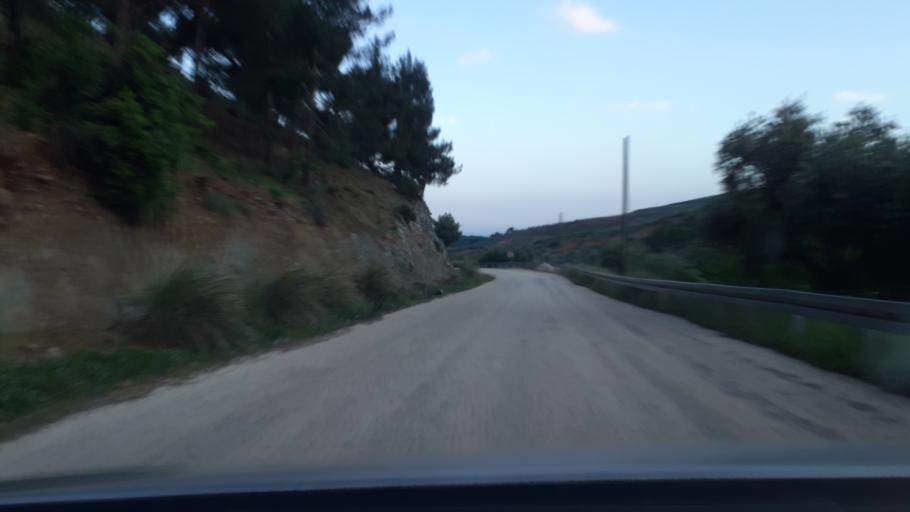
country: TR
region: Hatay
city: Kirikhan
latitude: 36.5183
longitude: 36.3184
